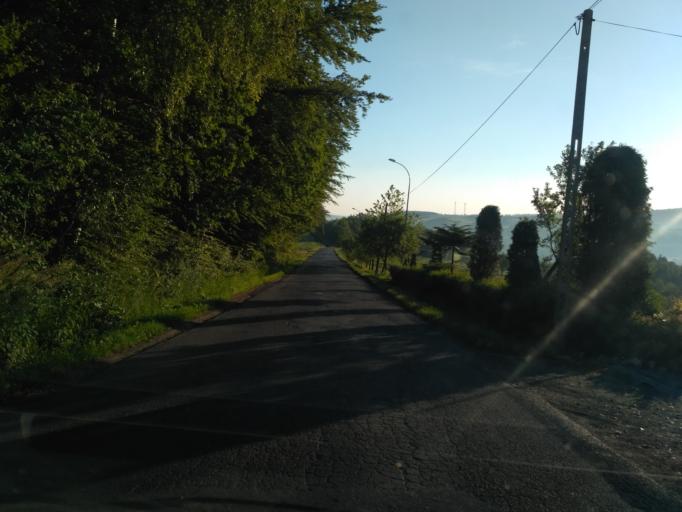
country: PL
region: Subcarpathian Voivodeship
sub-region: Powiat strzyzowski
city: Polomia
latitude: 49.8928
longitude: 21.8619
